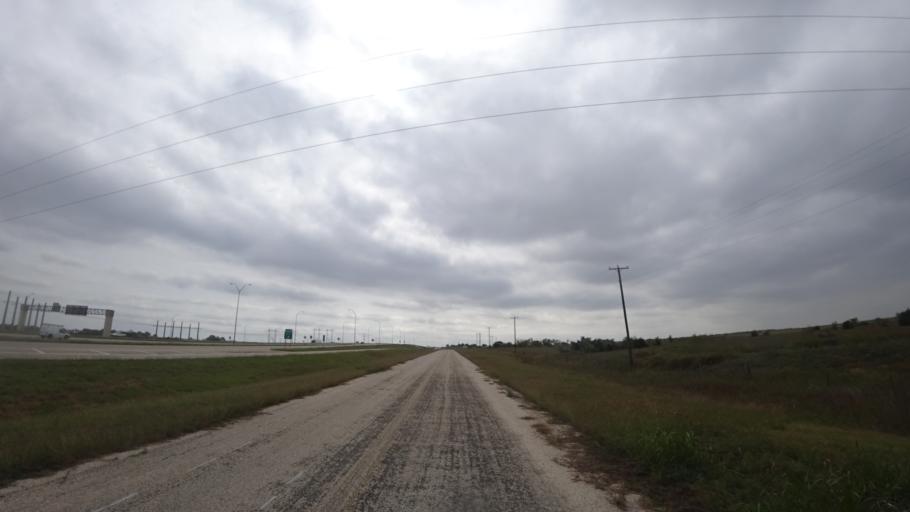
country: US
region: Texas
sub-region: Travis County
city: Pflugerville
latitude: 30.4096
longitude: -97.5853
